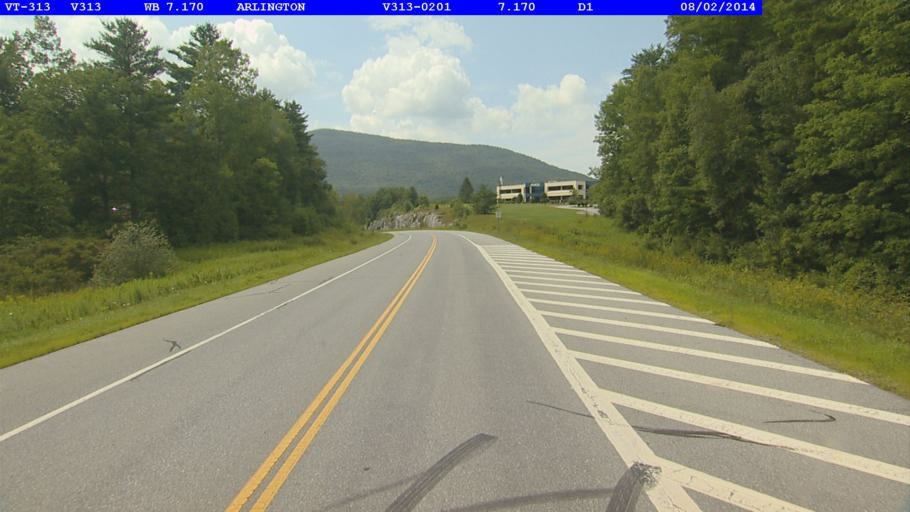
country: US
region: Vermont
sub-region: Bennington County
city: Arlington
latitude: 43.0543
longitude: -73.1529
